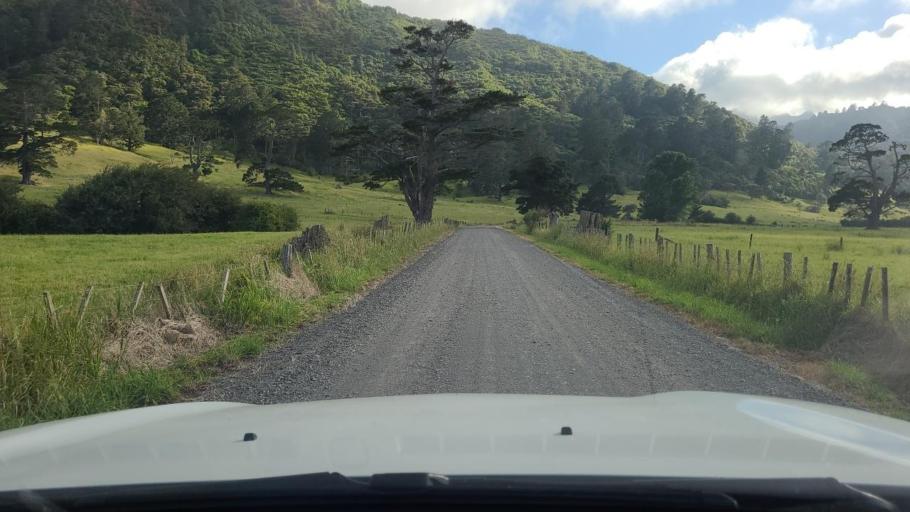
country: NZ
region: Bay of Plenty
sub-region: Western Bay of Plenty District
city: Katikati
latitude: -37.5624
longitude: 175.7443
